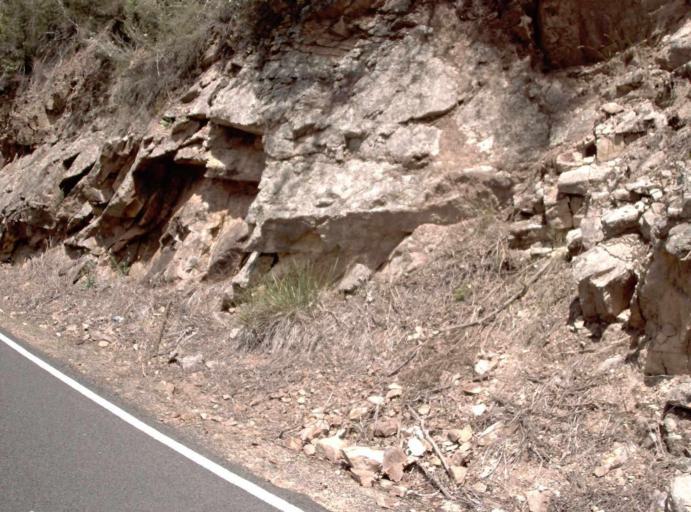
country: AU
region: Victoria
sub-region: East Gippsland
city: Lakes Entrance
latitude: -37.5523
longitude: 147.8769
